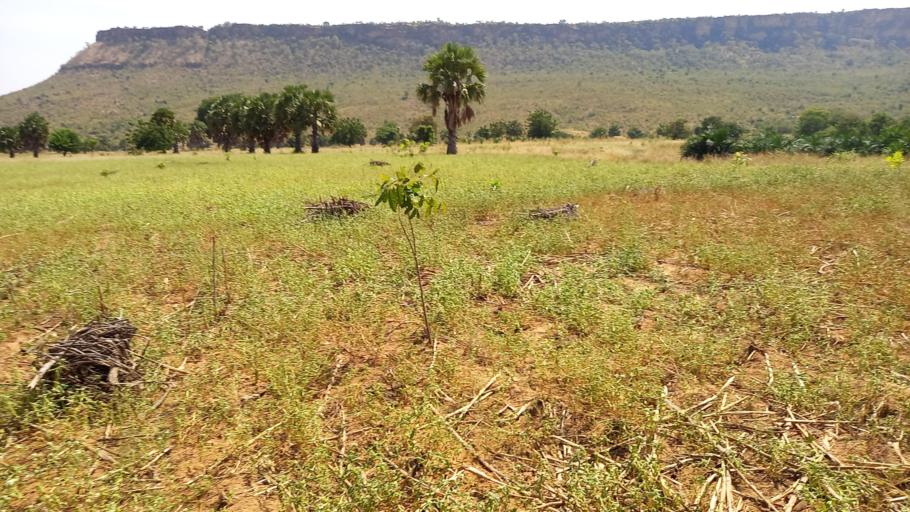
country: TG
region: Savanes
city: Dapaong
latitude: 10.8280
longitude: 0.3287
